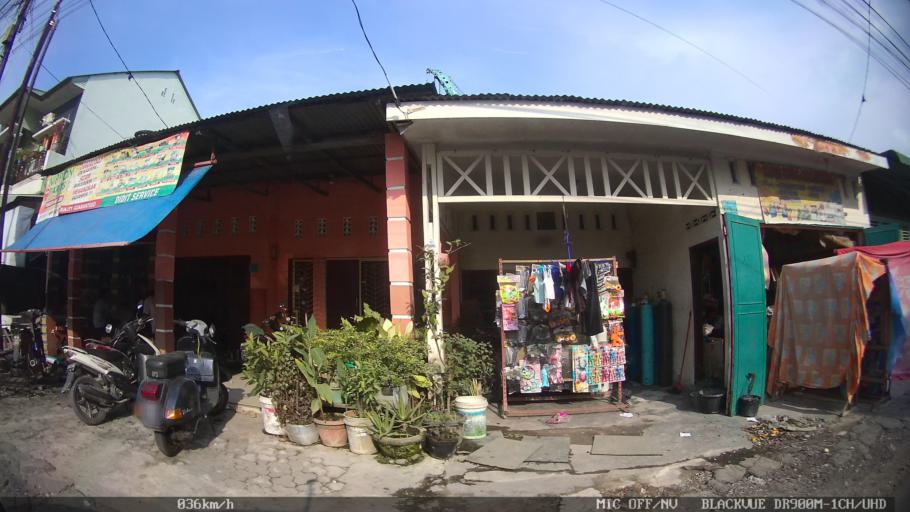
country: ID
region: North Sumatra
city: Medan
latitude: 3.6018
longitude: 98.7419
